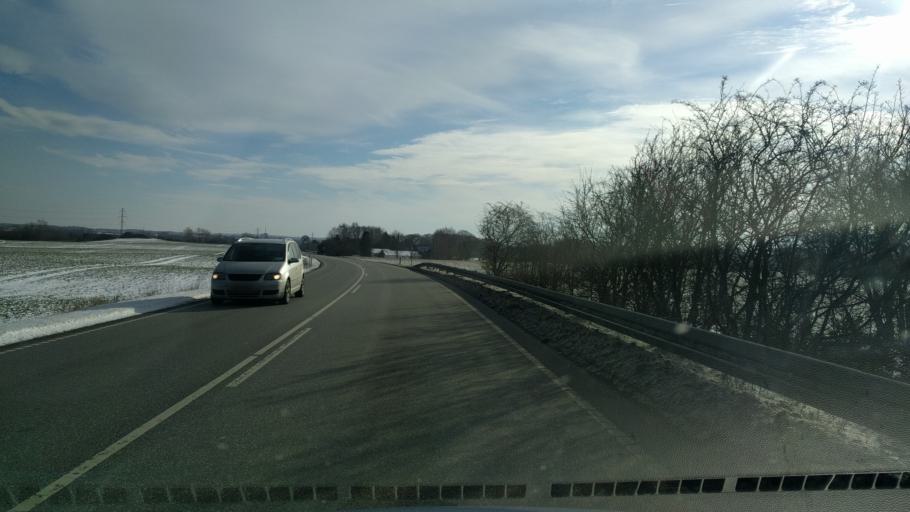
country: DK
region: Zealand
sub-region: Vordingborg Kommune
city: Neder Vindinge
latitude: 55.1448
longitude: 11.8991
